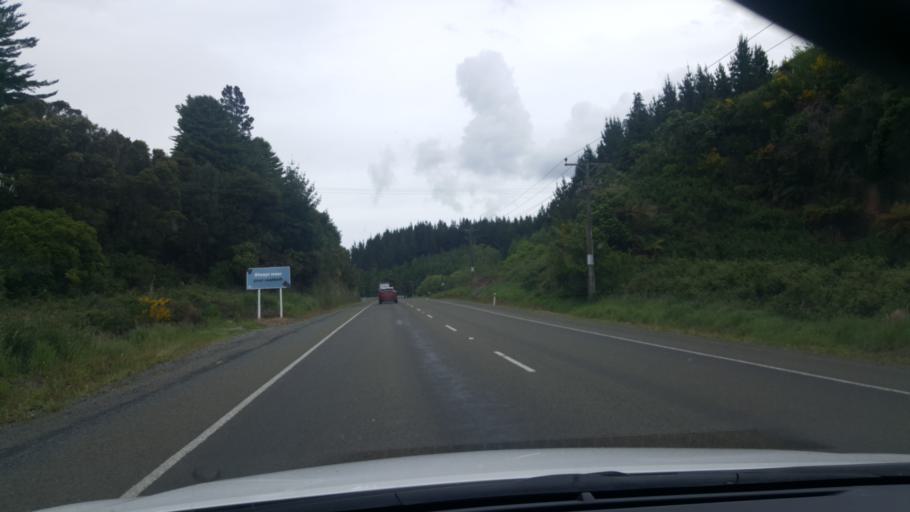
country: NZ
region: Bay of Plenty
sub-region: Rotorua District
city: Rotorua
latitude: -38.3238
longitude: 176.3713
